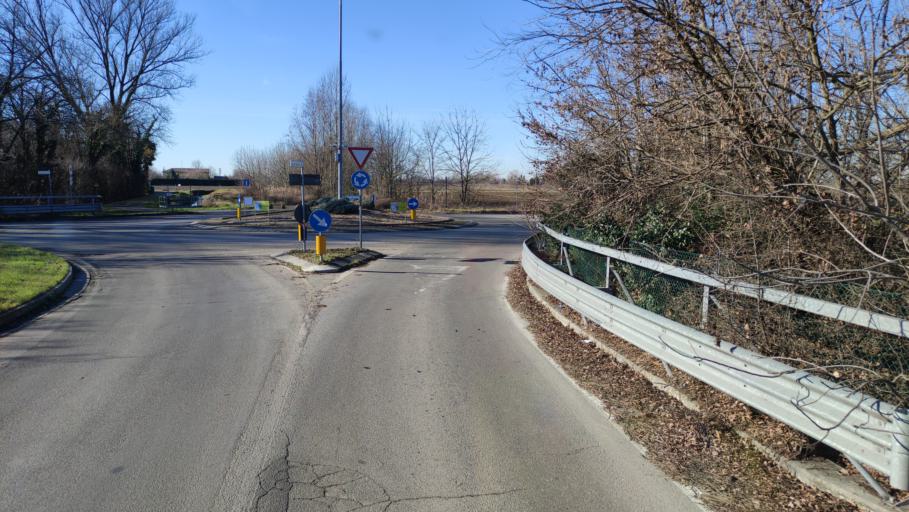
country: IT
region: Emilia-Romagna
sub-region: Provincia di Reggio Emilia
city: Correggio
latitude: 44.7819
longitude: 10.7792
